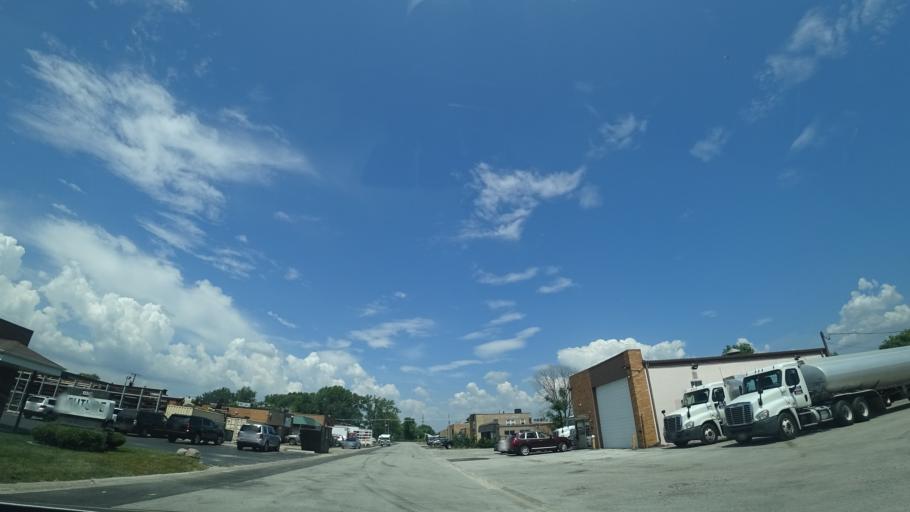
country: US
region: Illinois
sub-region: Cook County
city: Alsip
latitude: 41.6675
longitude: -87.7250
